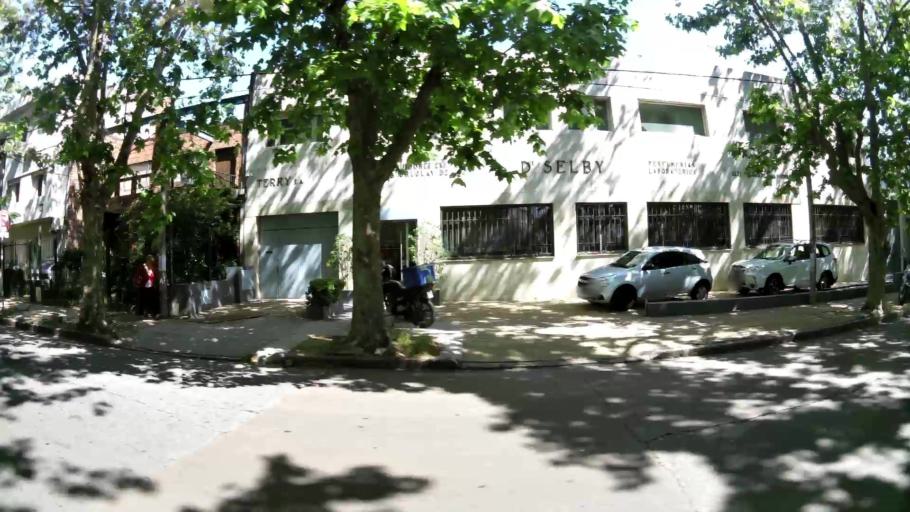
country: UY
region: Montevideo
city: Montevideo
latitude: -34.9027
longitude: -56.1444
